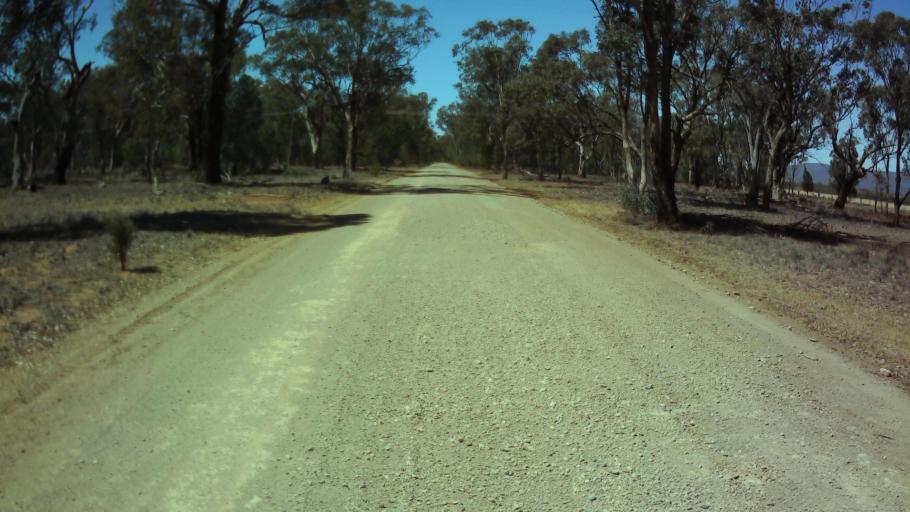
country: AU
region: New South Wales
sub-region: Weddin
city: Grenfell
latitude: -33.8534
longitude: 148.0878
